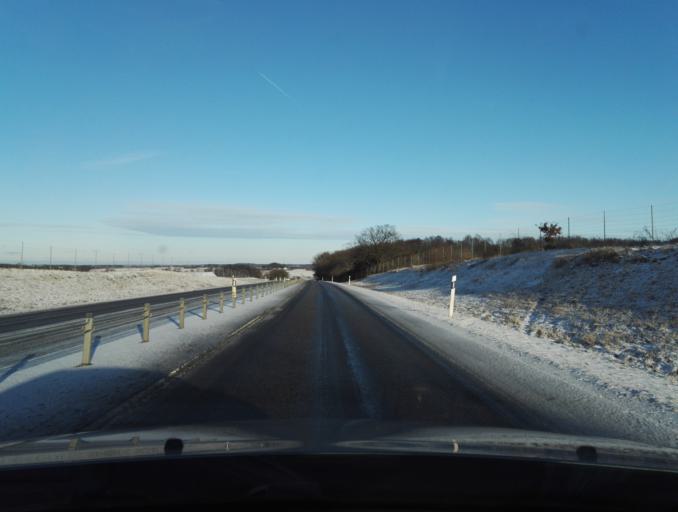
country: SE
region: Skane
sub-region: Svedala Kommun
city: Svedala
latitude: 55.4736
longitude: 13.2095
